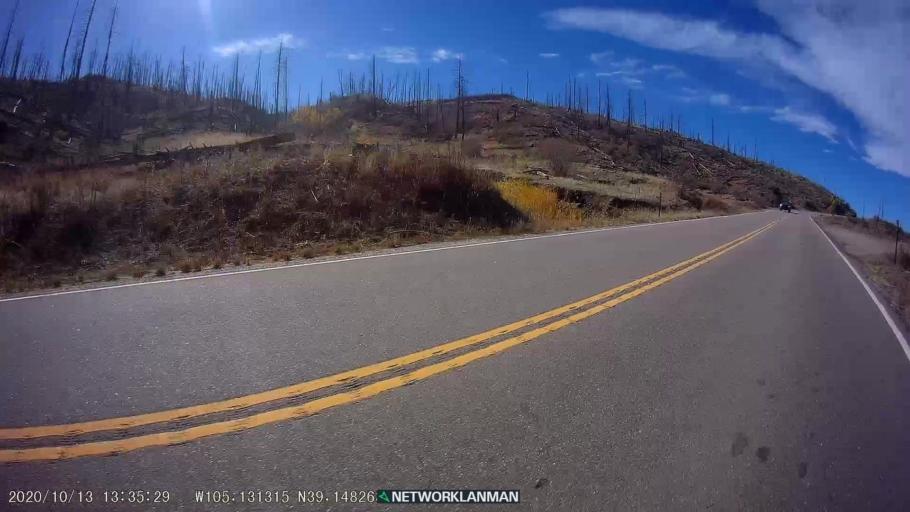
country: US
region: Colorado
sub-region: Teller County
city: Woodland Park
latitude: 39.1484
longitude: -105.1311
